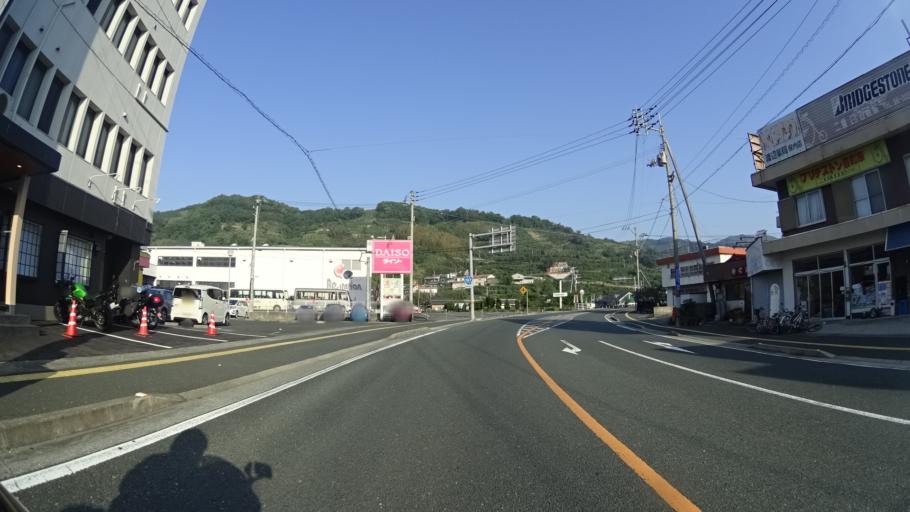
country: JP
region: Ehime
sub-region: Nishiuwa-gun
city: Ikata-cho
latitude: 33.4844
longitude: 132.3999
